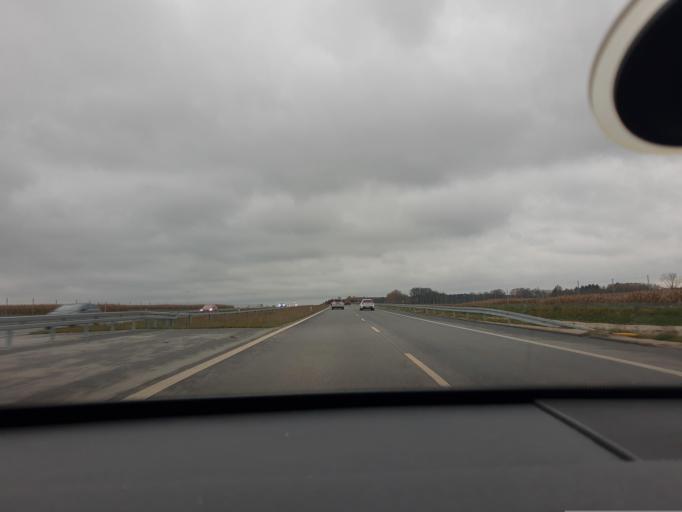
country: PL
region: Lodz Voivodeship
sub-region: Powiat pabianicki
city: Konstantynow Lodzki
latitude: 51.7122
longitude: 19.3464
